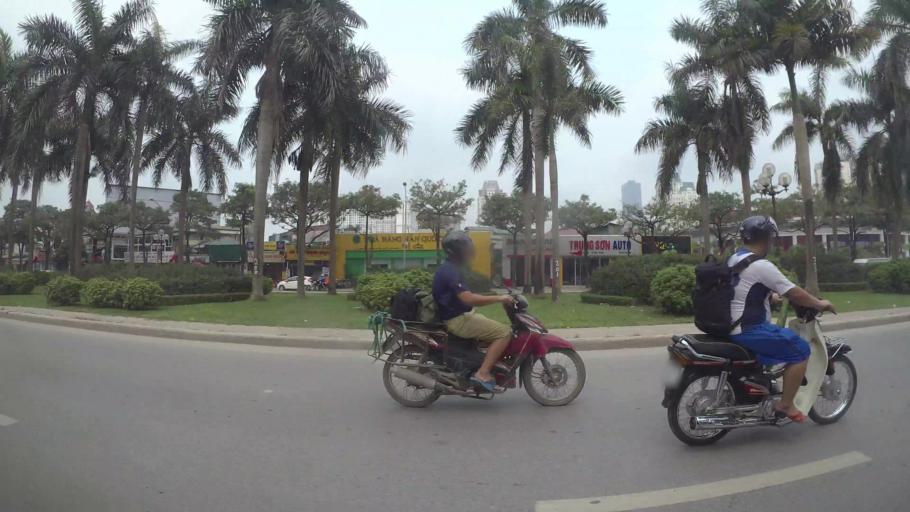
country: VN
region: Ha Noi
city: Cau Dien
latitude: 21.0129
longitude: 105.7703
